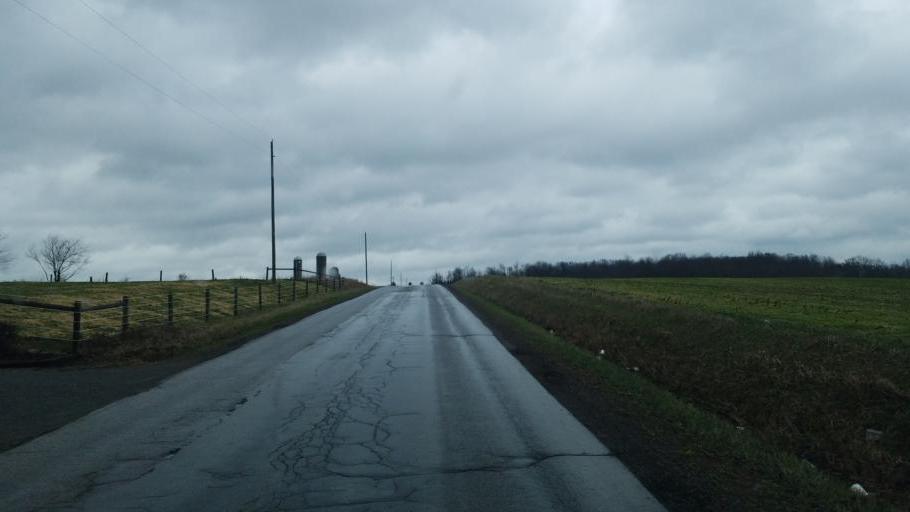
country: US
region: Ohio
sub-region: Wayne County
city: Apple Creek
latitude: 40.6784
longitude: -81.8178
